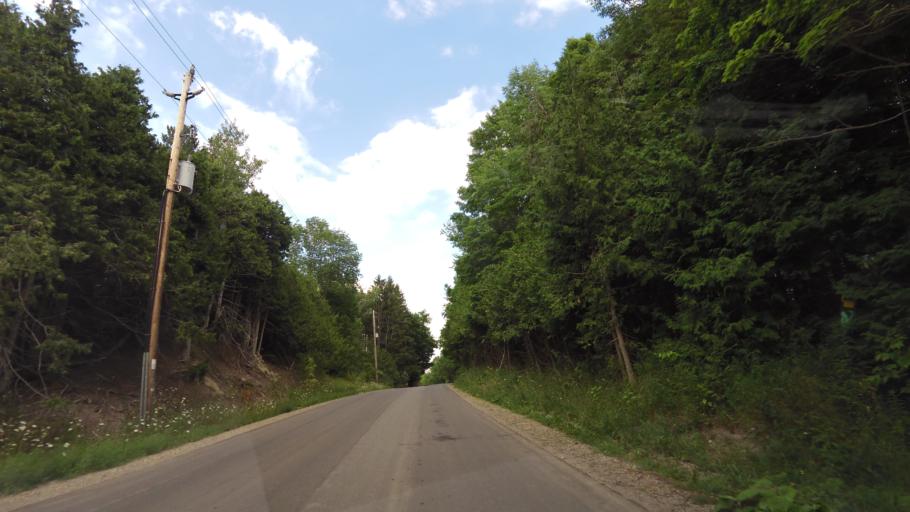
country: CA
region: Ontario
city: Orangeville
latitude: 43.9834
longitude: -79.9349
